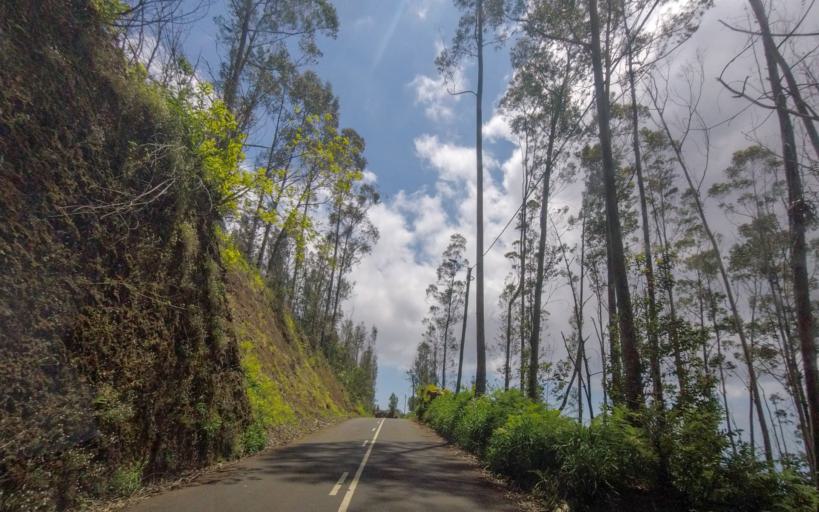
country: PT
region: Madeira
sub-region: Funchal
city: Nossa Senhora do Monte
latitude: 32.6818
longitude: -16.8837
